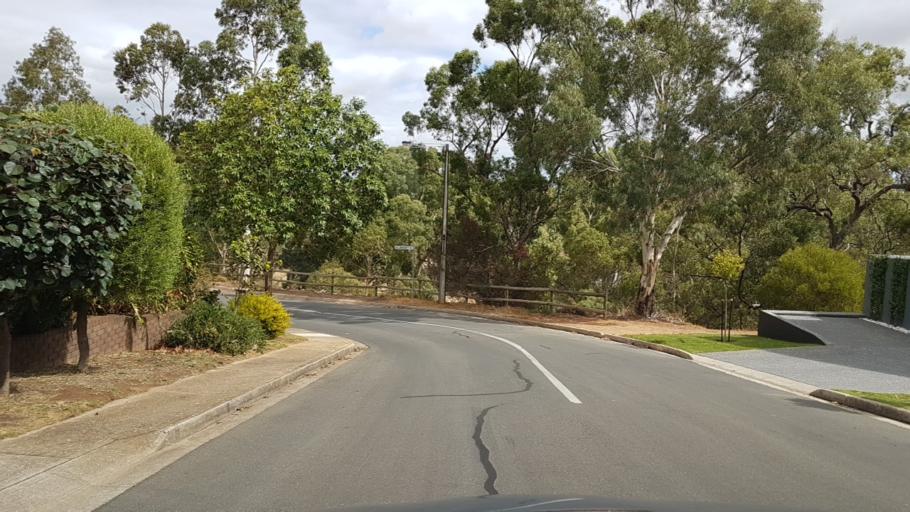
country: AU
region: South Australia
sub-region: Gawler
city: Gawler
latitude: -34.6076
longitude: 138.7520
